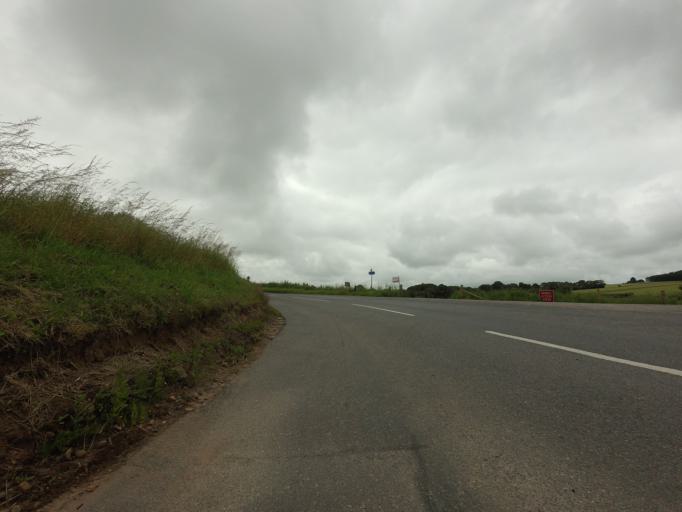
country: GB
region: Scotland
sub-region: Aberdeenshire
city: Turriff
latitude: 57.5439
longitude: -2.3397
